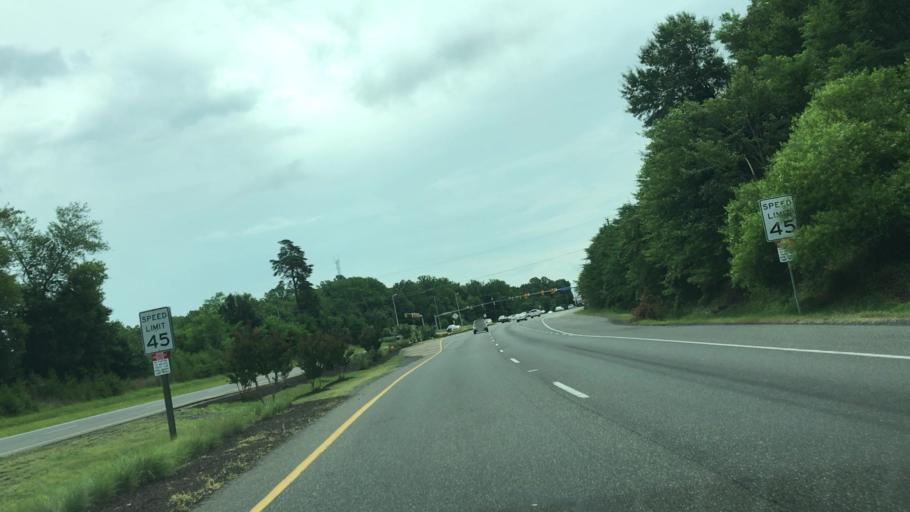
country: US
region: Virginia
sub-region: Prince William County
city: Lake Ridge
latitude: 38.6819
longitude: -77.3627
